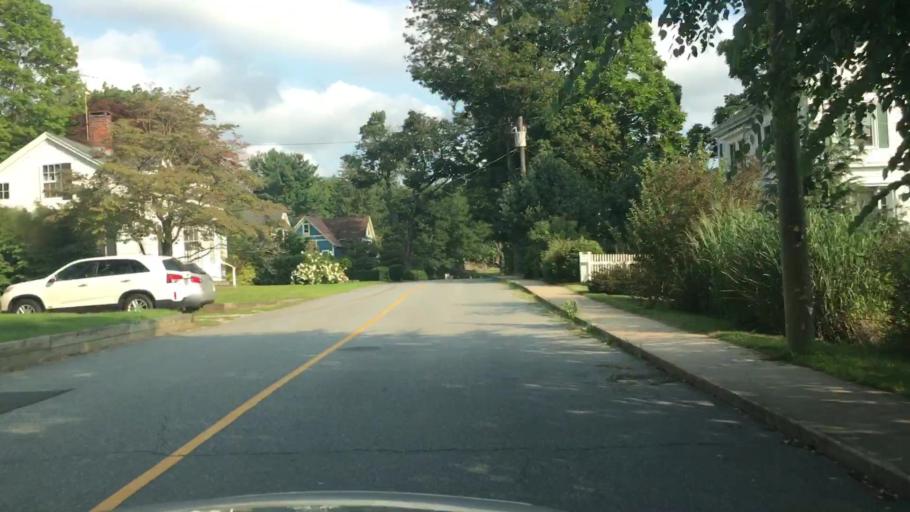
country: US
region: Connecticut
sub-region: Middlesex County
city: Deep River Center
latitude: 41.3875
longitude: -72.4340
